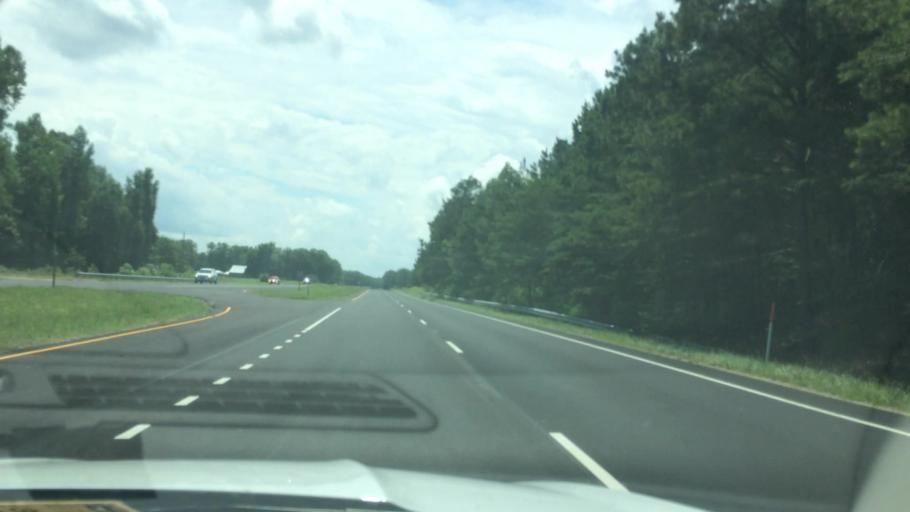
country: US
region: Virginia
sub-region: Middlesex County
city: Saluda
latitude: 37.5526
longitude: -76.6774
